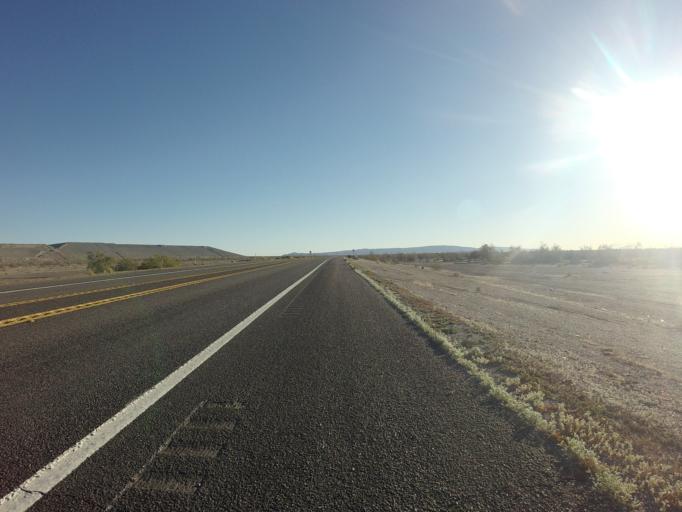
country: MX
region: Baja California
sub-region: Mexicali
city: Ejido Netzahualcoyotl
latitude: 33.0176
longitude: -114.9890
